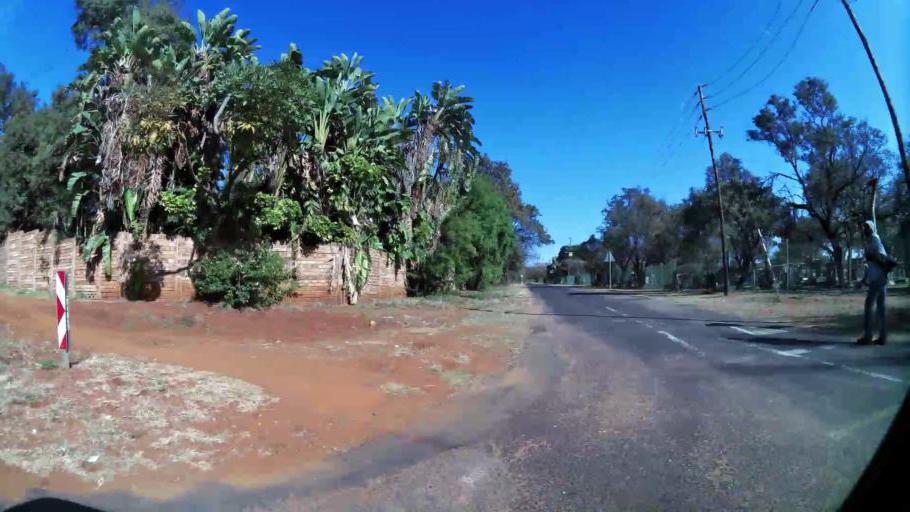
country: ZA
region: Gauteng
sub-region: City of Tshwane Metropolitan Municipality
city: Pretoria
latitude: -25.6803
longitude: 28.1340
